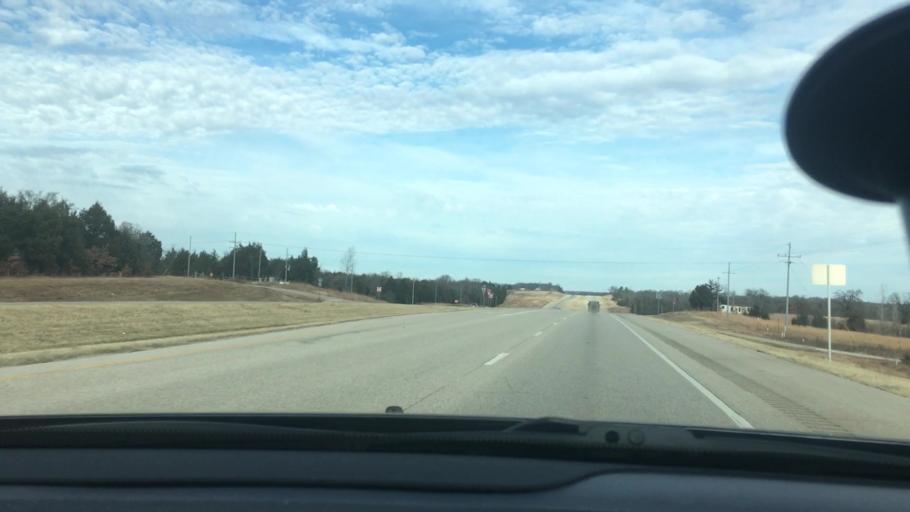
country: US
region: Oklahoma
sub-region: Pontotoc County
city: Byng
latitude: 34.9037
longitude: -96.6759
